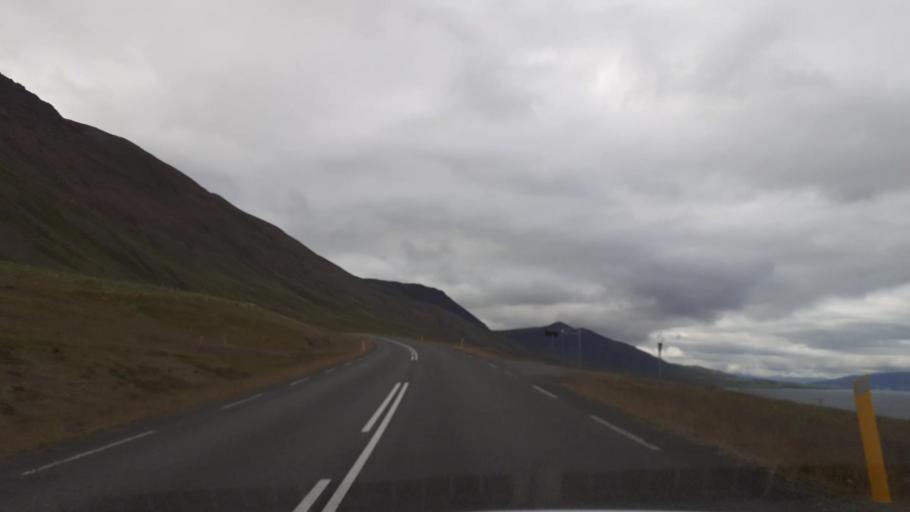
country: IS
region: Northeast
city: Akureyri
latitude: 65.8633
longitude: -18.0720
